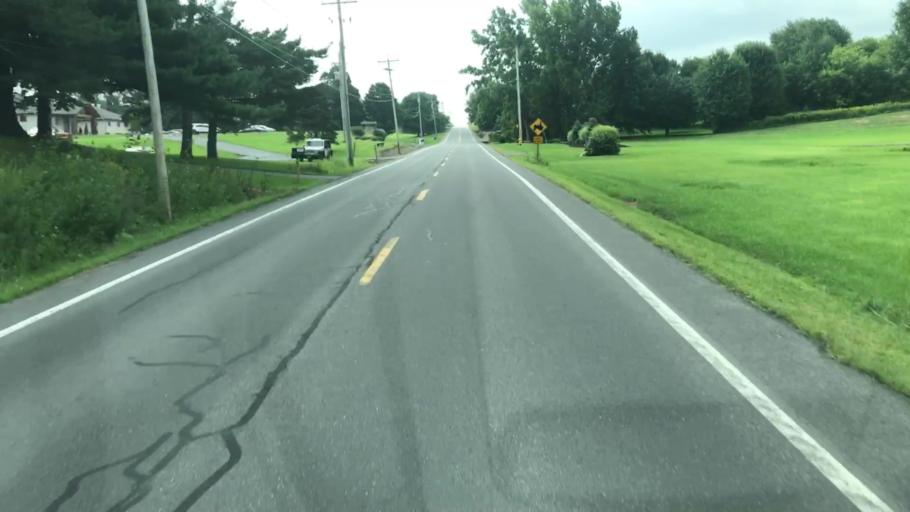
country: US
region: New York
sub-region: Onondaga County
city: Peru
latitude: 43.0479
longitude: -76.3661
